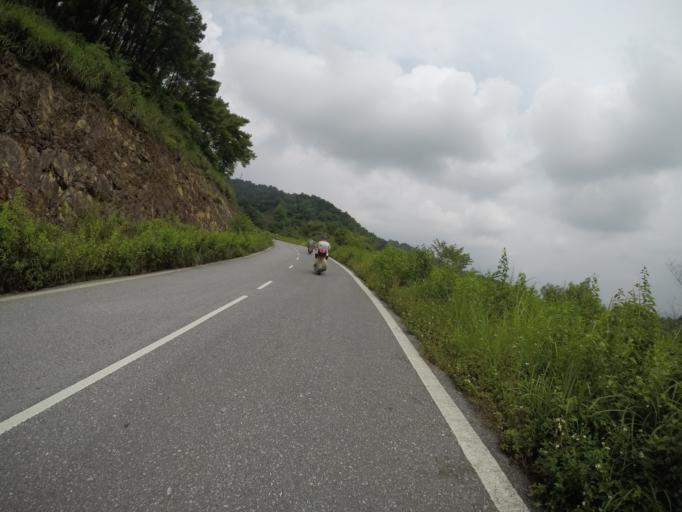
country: VN
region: Ha Noi
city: Soc Son
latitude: 21.2825
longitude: 105.8250
